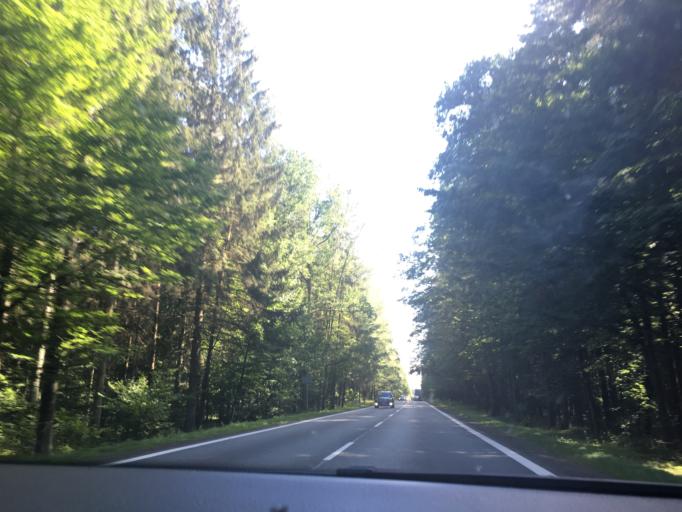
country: PL
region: Podlasie
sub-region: Powiat bialostocki
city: Wasilkow
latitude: 53.2894
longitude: 23.1228
